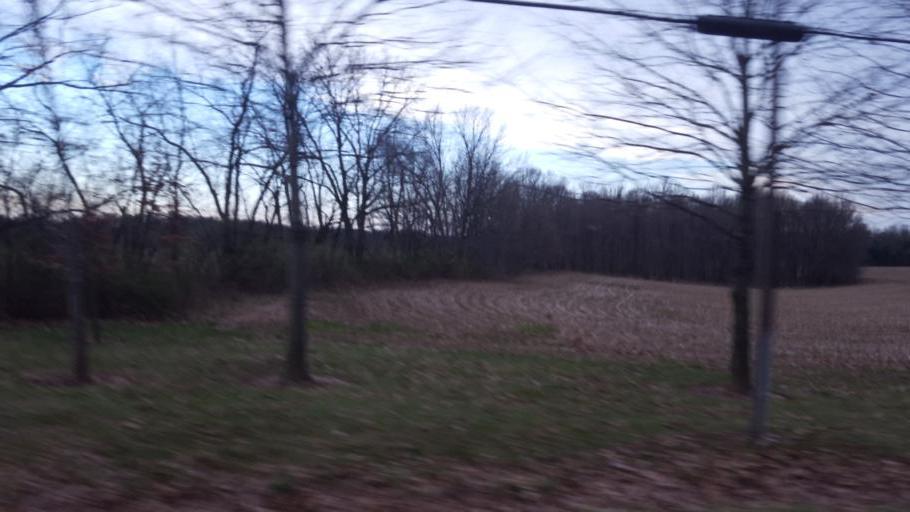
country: US
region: Ohio
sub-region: Knox County
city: Fredericktown
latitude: 40.4927
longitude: -82.4984
